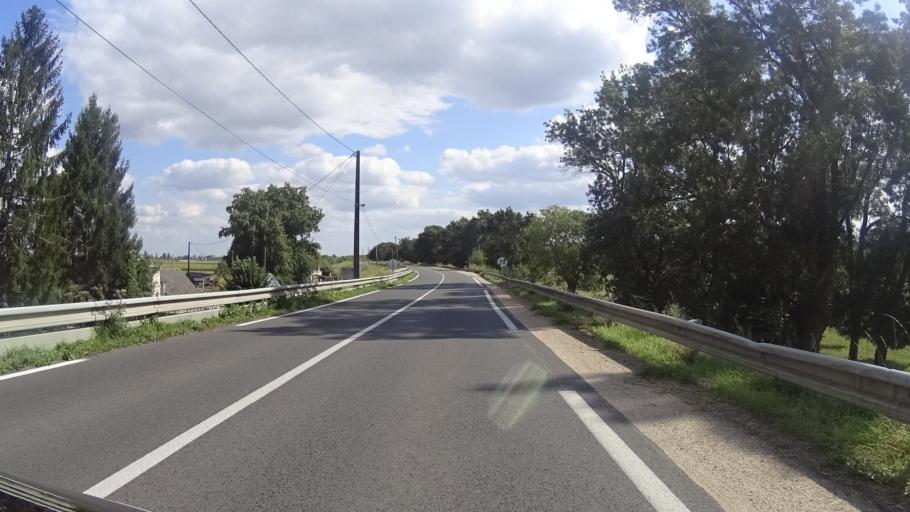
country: FR
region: Pays de la Loire
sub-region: Departement de Maine-et-Loire
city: Saint-Mathurin-sur-Loire
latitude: 47.4084
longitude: -0.2966
